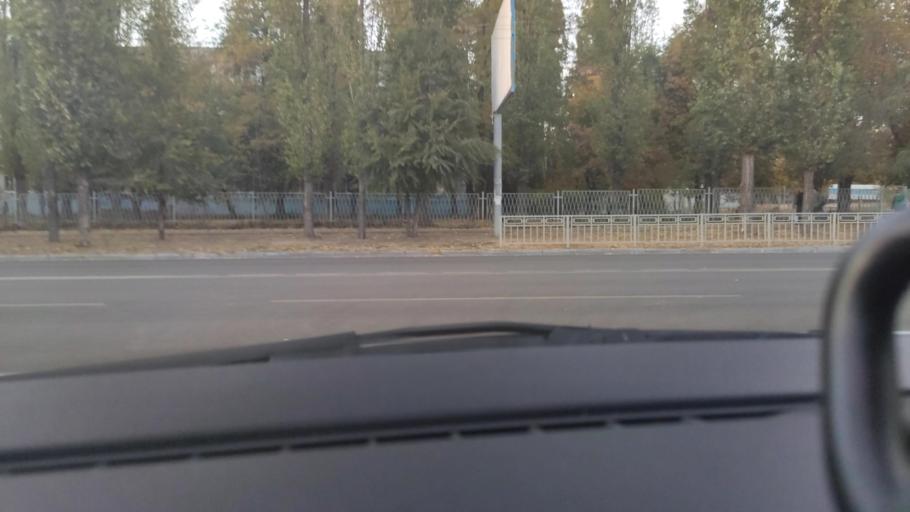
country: RU
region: Voronezj
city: Voronezh
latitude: 51.7020
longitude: 39.1684
